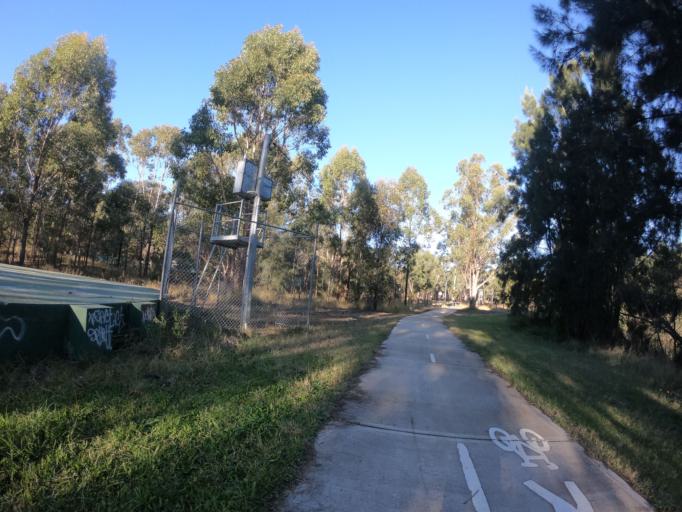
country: AU
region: New South Wales
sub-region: Hawkesbury
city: South Windsor
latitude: -33.6353
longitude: 150.8110
